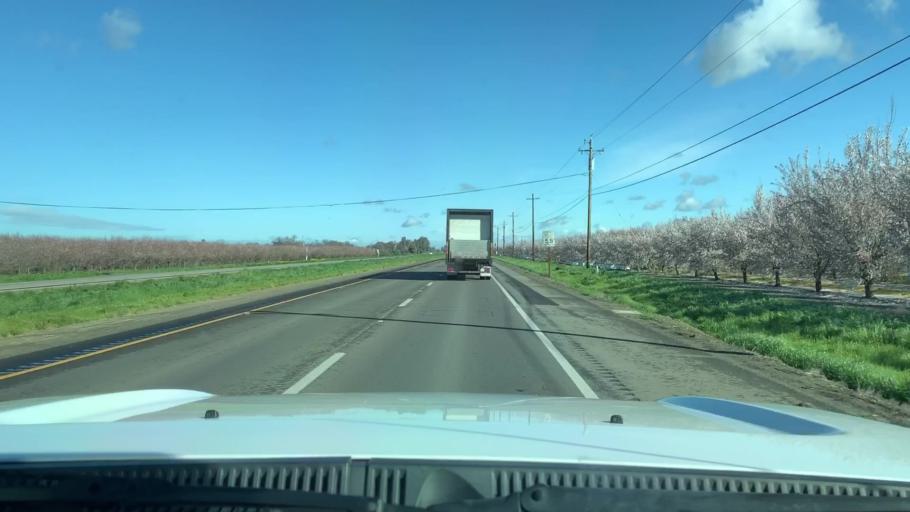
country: US
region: California
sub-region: Kings County
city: Lemoore
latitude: 36.3456
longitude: -119.8079
